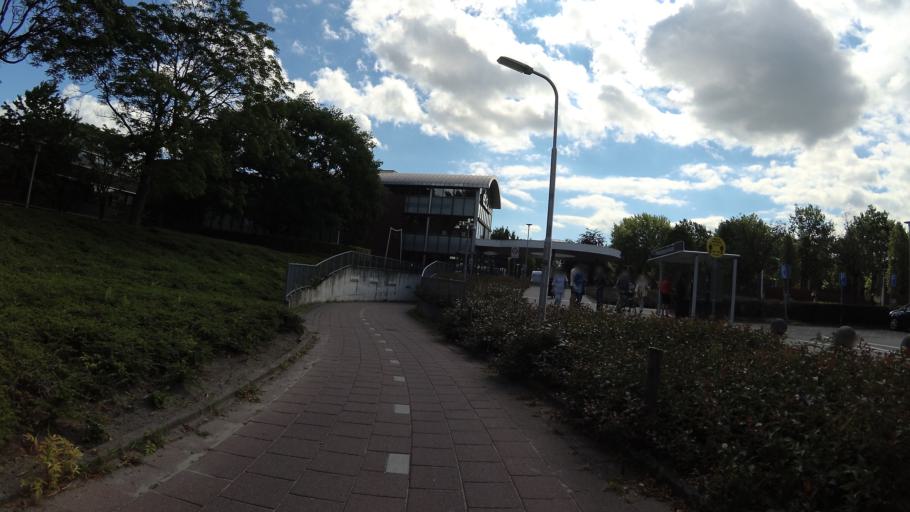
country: NL
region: North Brabant
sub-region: Gemeente Tilburg
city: Tilburg
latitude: 51.5393
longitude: 5.1025
